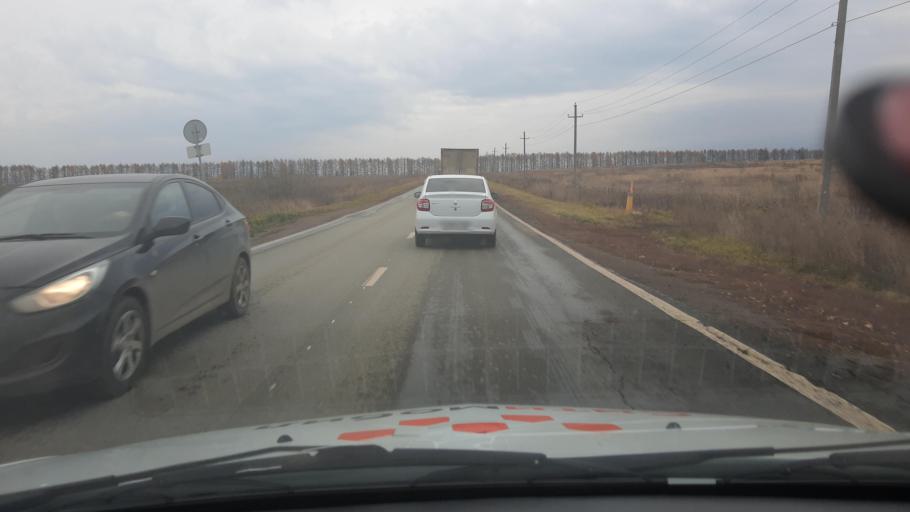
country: RU
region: Bashkortostan
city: Iglino
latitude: 54.7397
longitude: 56.2449
